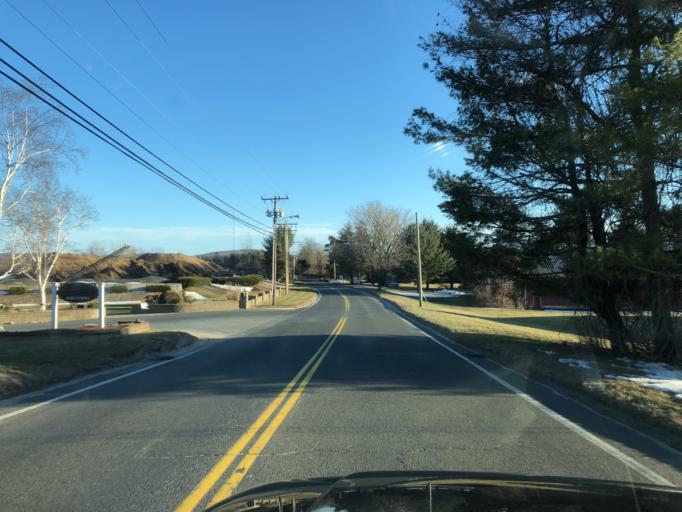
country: US
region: Connecticut
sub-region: Hartford County
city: Farmington
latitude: 41.7478
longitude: -72.8546
